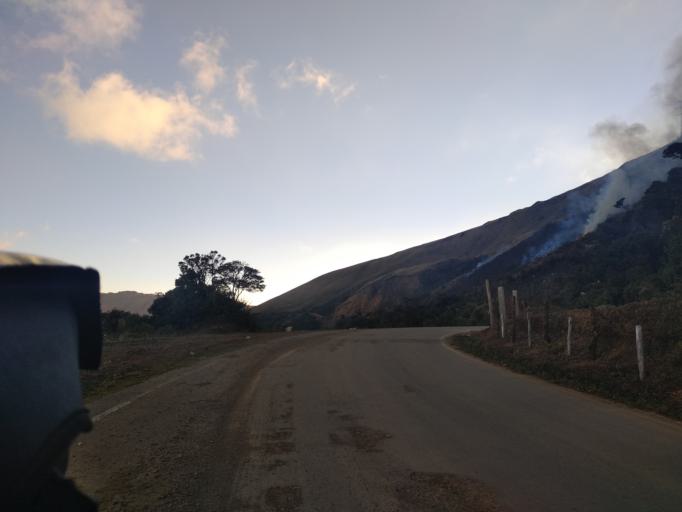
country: PE
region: Amazonas
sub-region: Provincia de Chachapoyas
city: Montevideo
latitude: -6.7195
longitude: -77.8750
